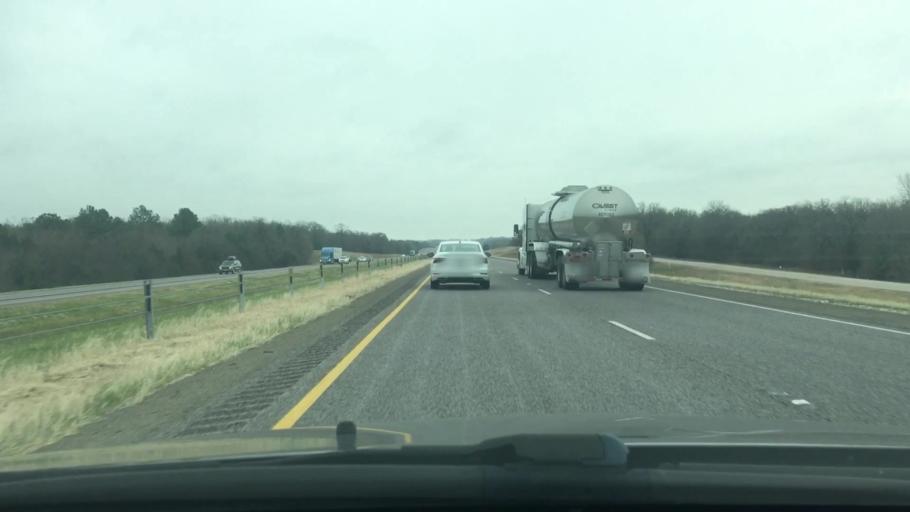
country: US
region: Texas
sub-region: Freestone County
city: Fairfield
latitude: 31.7590
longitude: -96.2081
